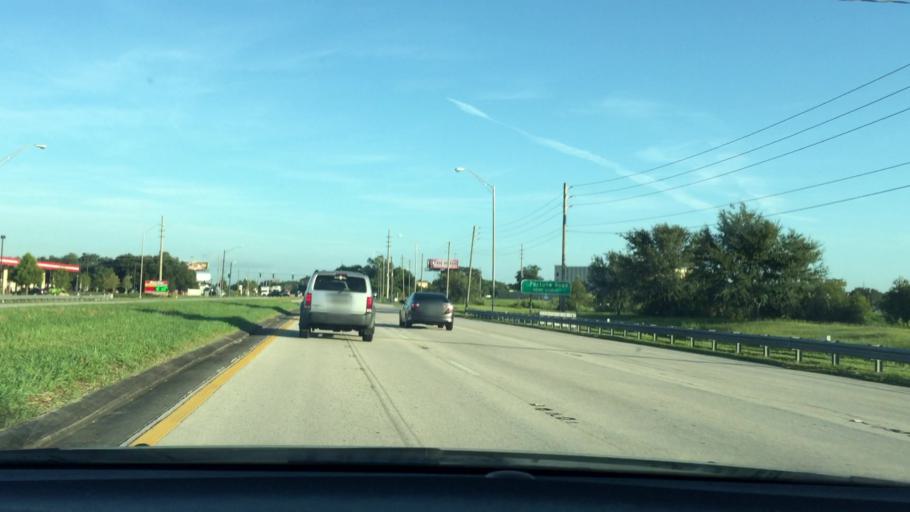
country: US
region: Florida
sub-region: Osceola County
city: Buenaventura Lakes
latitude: 28.2989
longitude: -81.3724
